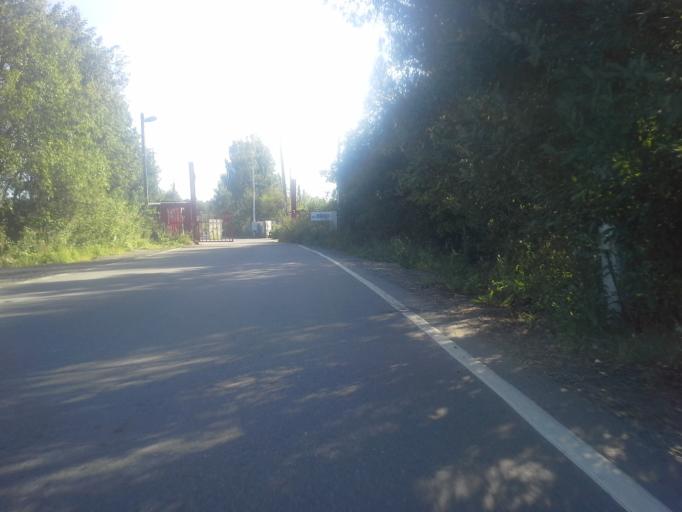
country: RU
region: Moskovskaya
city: Kievskij
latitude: 55.3546
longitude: 36.9521
